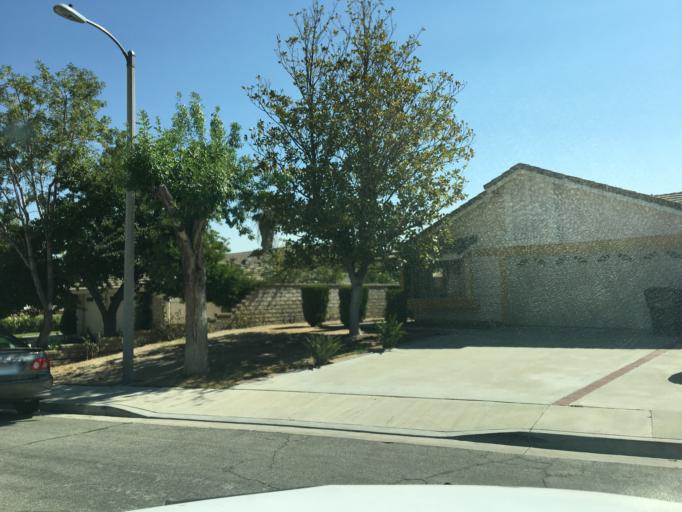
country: US
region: California
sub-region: Los Angeles County
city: Castaic
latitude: 34.4874
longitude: -118.6245
